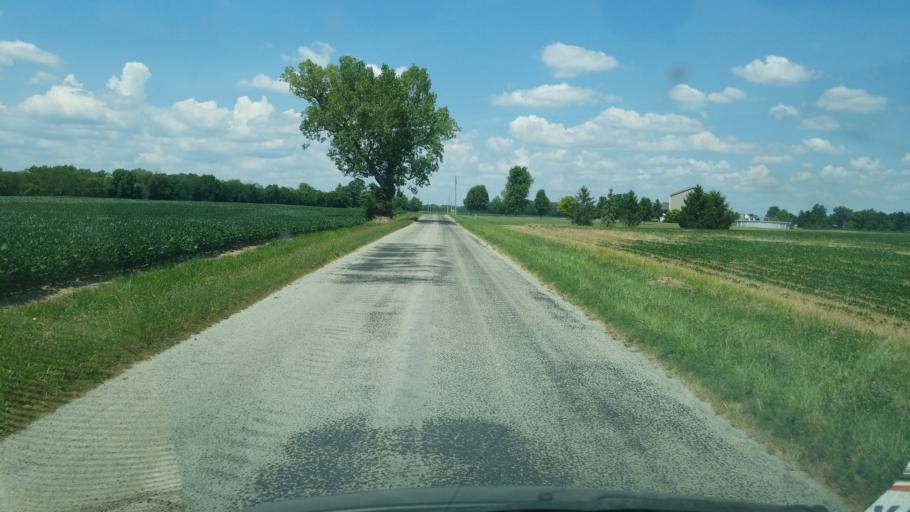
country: US
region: Ohio
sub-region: Madison County
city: Plain City
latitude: 40.0684
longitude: -83.3996
